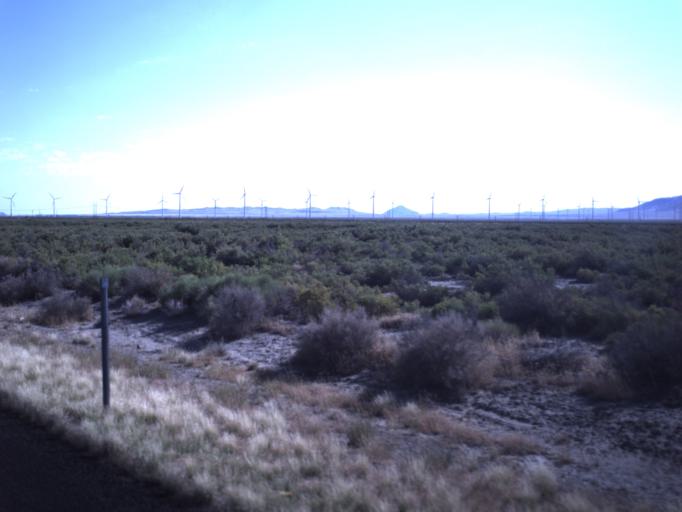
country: US
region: Utah
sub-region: Beaver County
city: Milford
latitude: 38.5573
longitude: -112.9912
